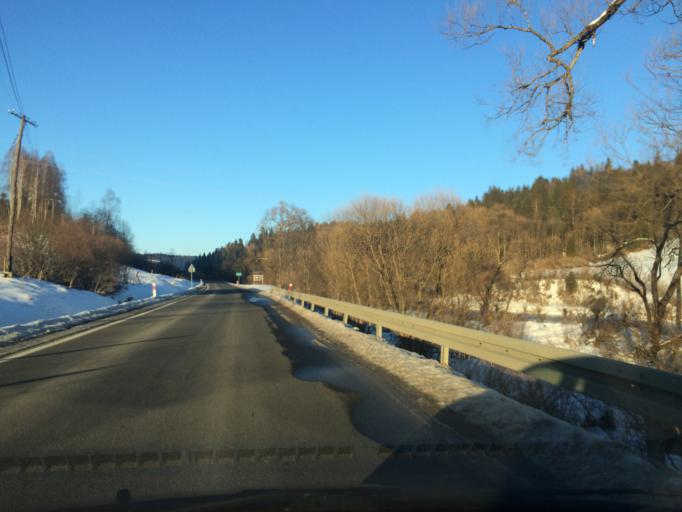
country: PL
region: Subcarpathian Voivodeship
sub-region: Powiat bieszczadzki
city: Lutowiska
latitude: 49.2160
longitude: 22.6915
